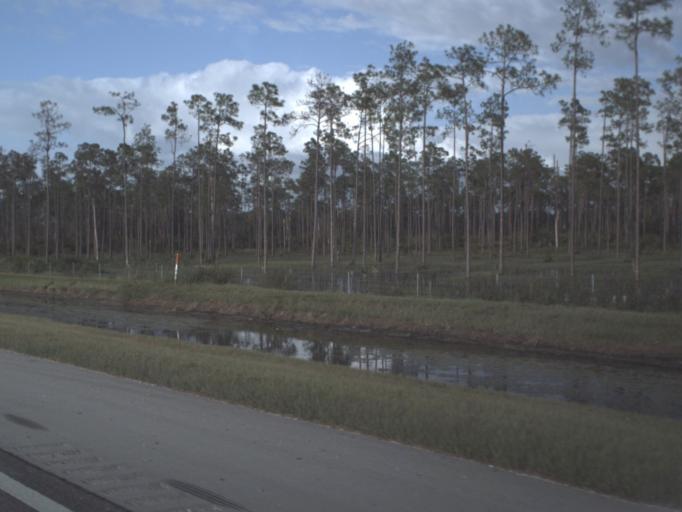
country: US
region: Florida
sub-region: Lee County
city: Three Oaks
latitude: 26.5050
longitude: -81.7939
